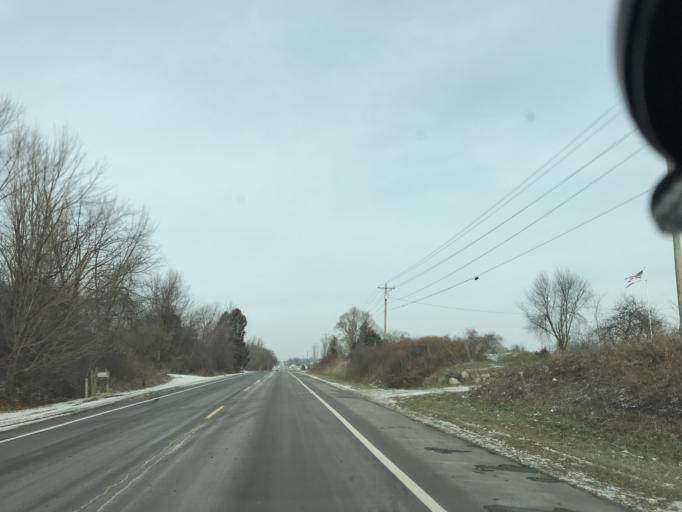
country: US
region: Michigan
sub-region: Ionia County
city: Lake Odessa
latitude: 42.7908
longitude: -85.0744
